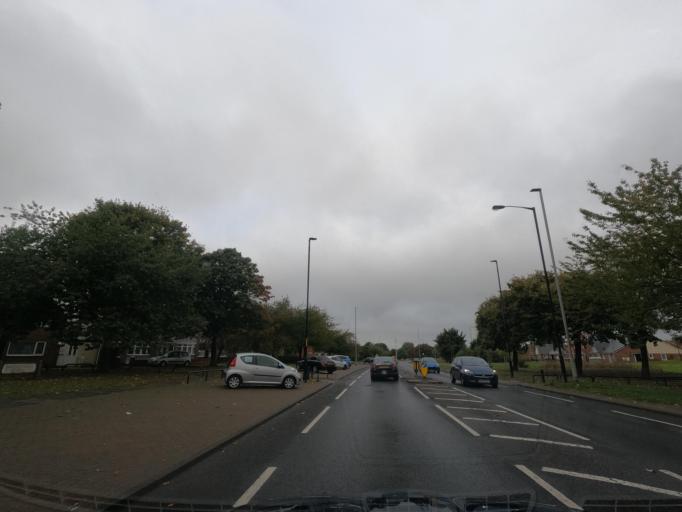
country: GB
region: England
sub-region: Middlesbrough
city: Nunthorpe
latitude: 54.5550
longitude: -1.1853
